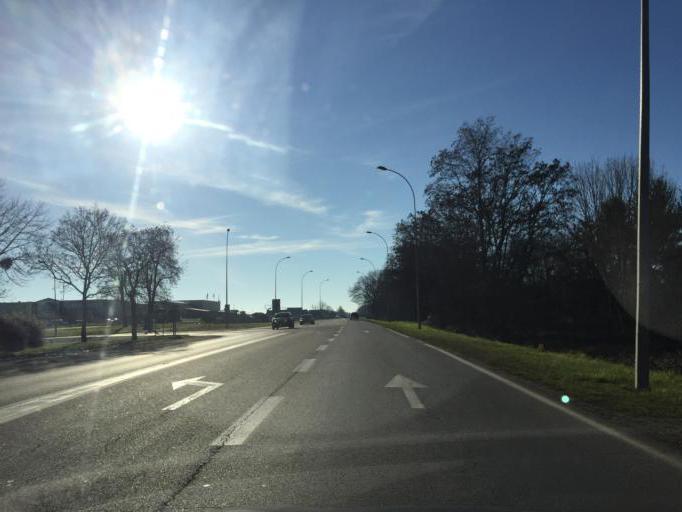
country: FR
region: Auvergne
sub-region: Departement de l'Allier
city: Saint-Pourcain-sur-Sioule
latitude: 46.2989
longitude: 3.2957
